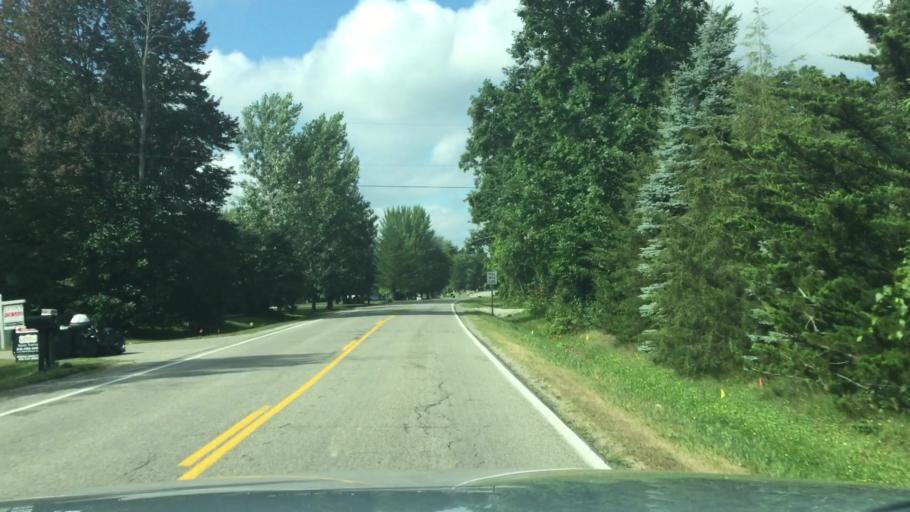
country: US
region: Michigan
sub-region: Genesee County
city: Clio
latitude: 43.2131
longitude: -83.7051
